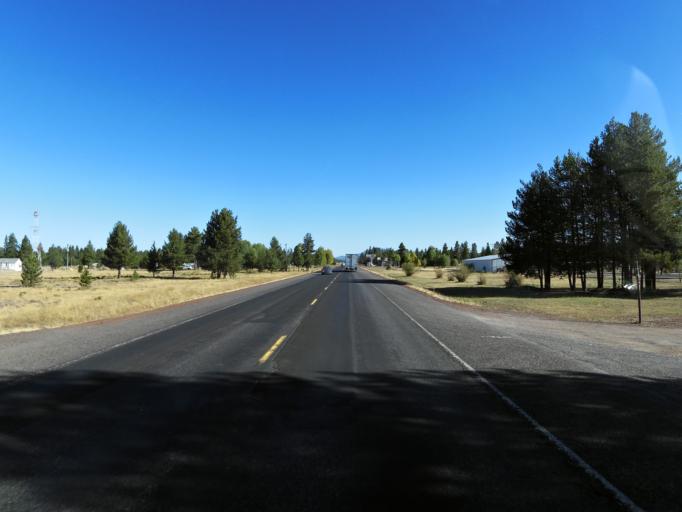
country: US
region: Oregon
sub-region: Deschutes County
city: La Pine
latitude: 43.1313
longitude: -121.8042
